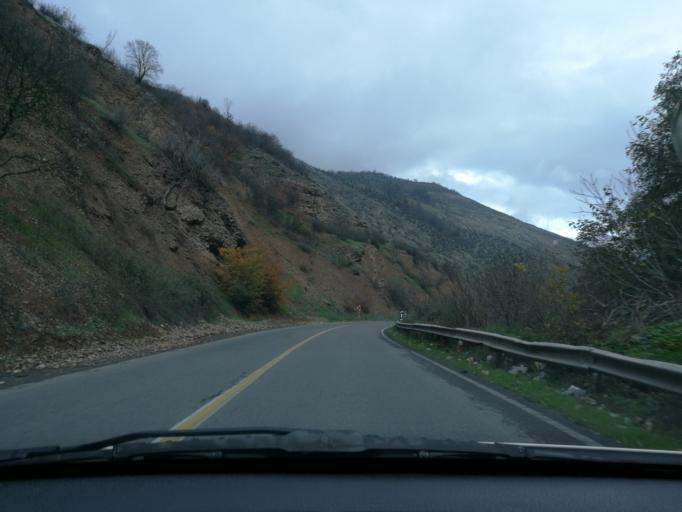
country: IR
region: Mazandaran
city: Chalus
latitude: 36.3649
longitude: 51.2615
